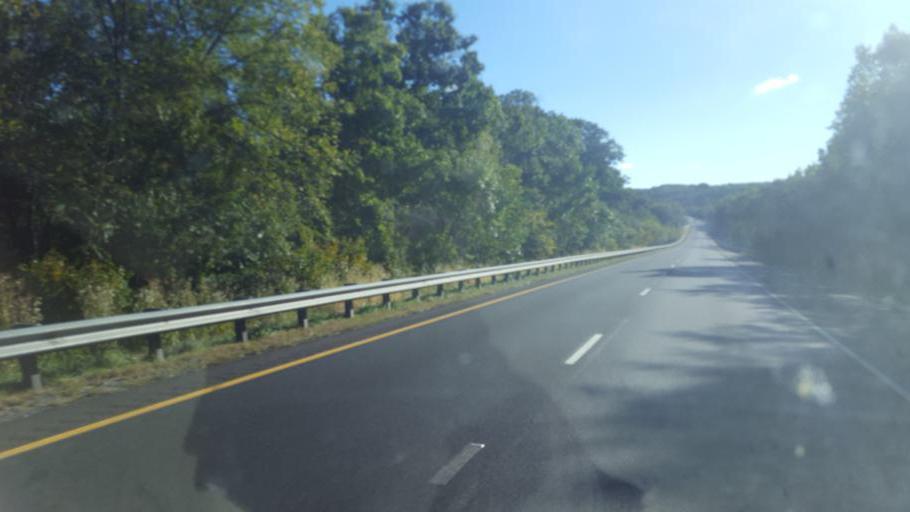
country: US
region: Maryland
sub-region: Washington County
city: Wilson-Conococheague
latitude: 39.6272
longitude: -77.9803
